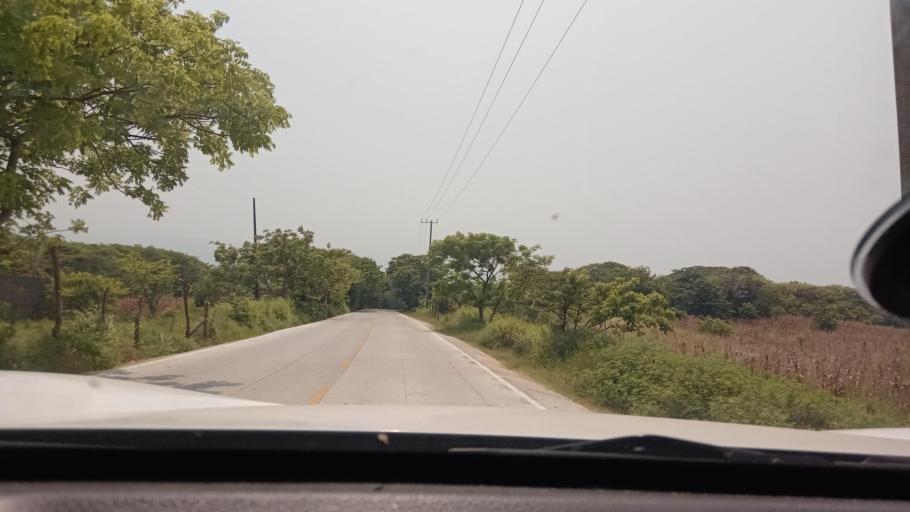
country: MX
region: Veracruz
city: Catemaco
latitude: 18.5562
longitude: -95.0004
